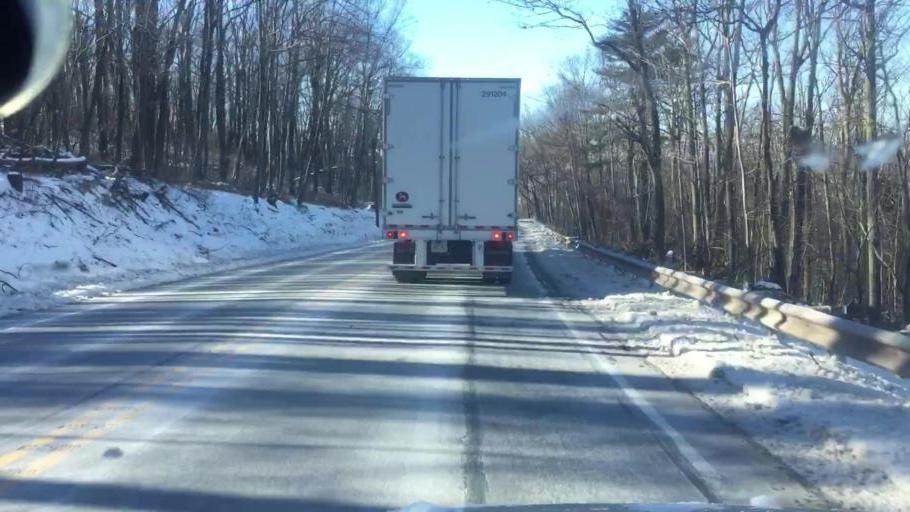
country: US
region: Pennsylvania
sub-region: Luzerne County
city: Conyngham
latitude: 41.0335
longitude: -76.1167
